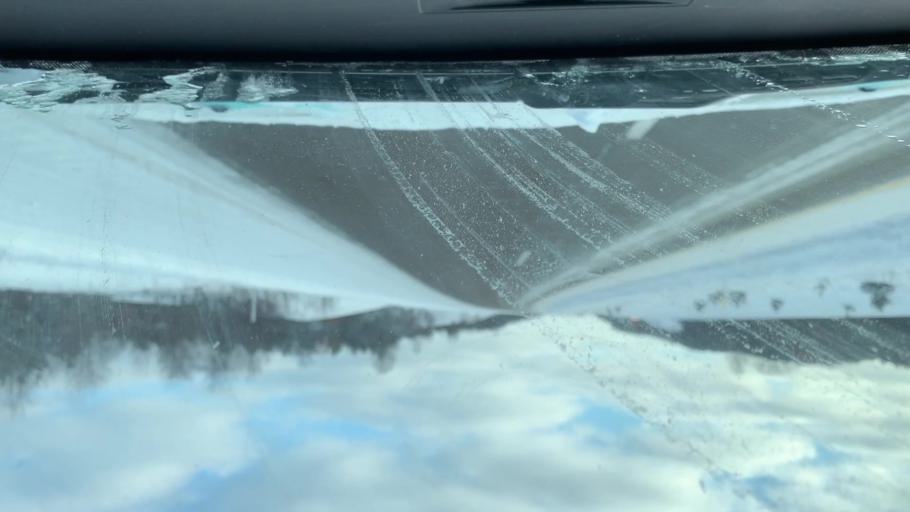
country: US
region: Michigan
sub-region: Wexford County
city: Manton
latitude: 44.3670
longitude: -85.4022
